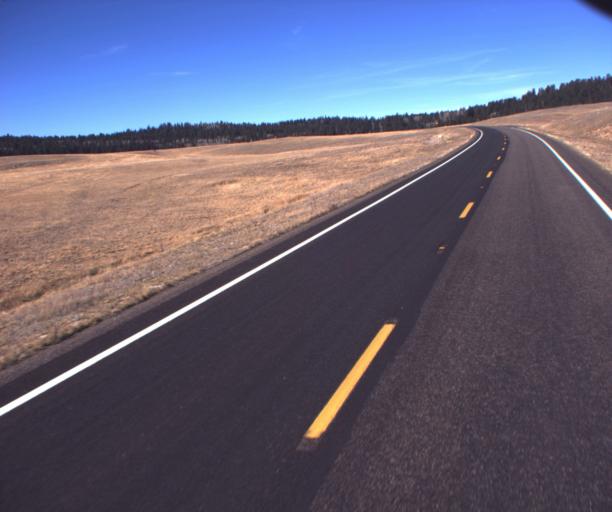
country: US
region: Arizona
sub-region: Coconino County
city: Grand Canyon
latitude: 36.4944
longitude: -112.1319
